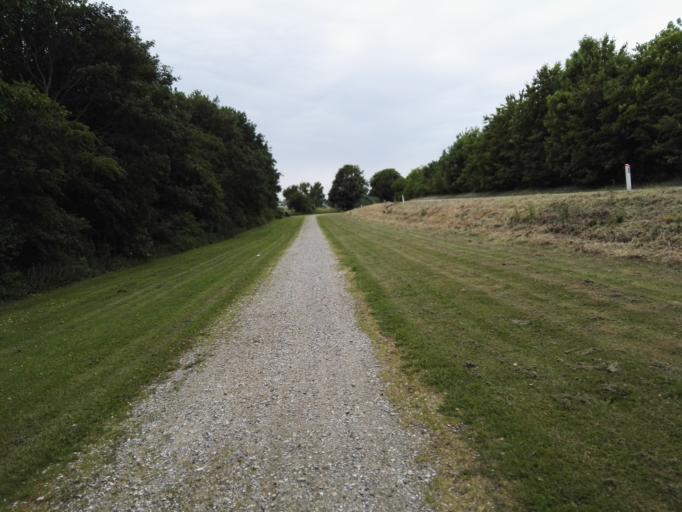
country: DK
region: Zealand
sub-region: Roskilde Kommune
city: Jyllinge
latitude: 55.7759
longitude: 12.1269
